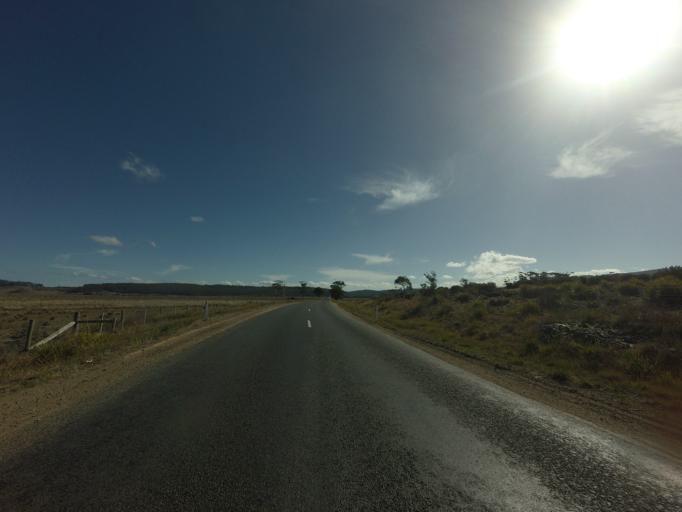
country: AU
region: Tasmania
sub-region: Break O'Day
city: St Helens
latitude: -41.9488
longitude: 148.1992
